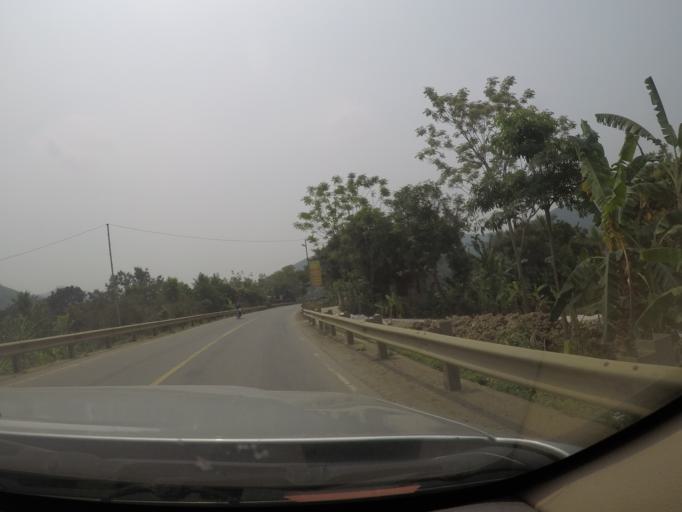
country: VN
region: Thanh Hoa
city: Thi Tran Cam Thuy
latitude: 20.1929
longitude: 105.4782
